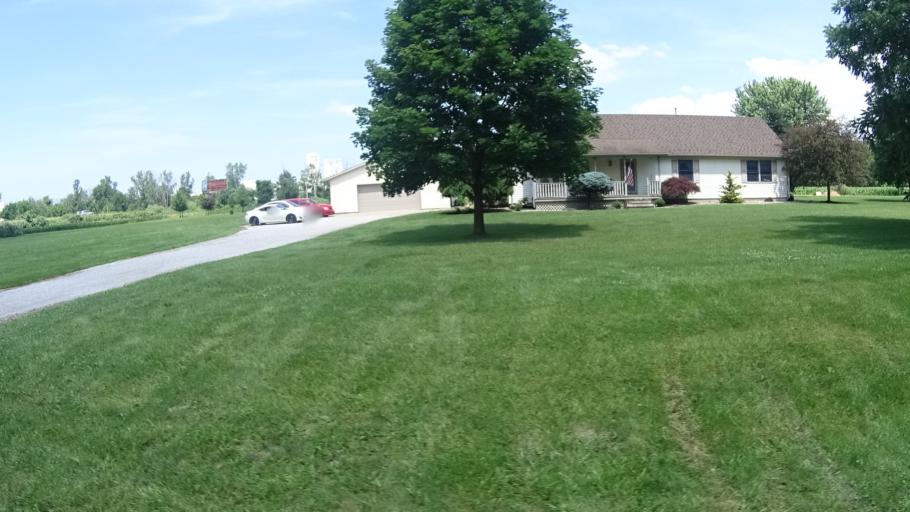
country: US
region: Ohio
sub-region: Erie County
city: Huron
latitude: 41.3677
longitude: -82.5410
